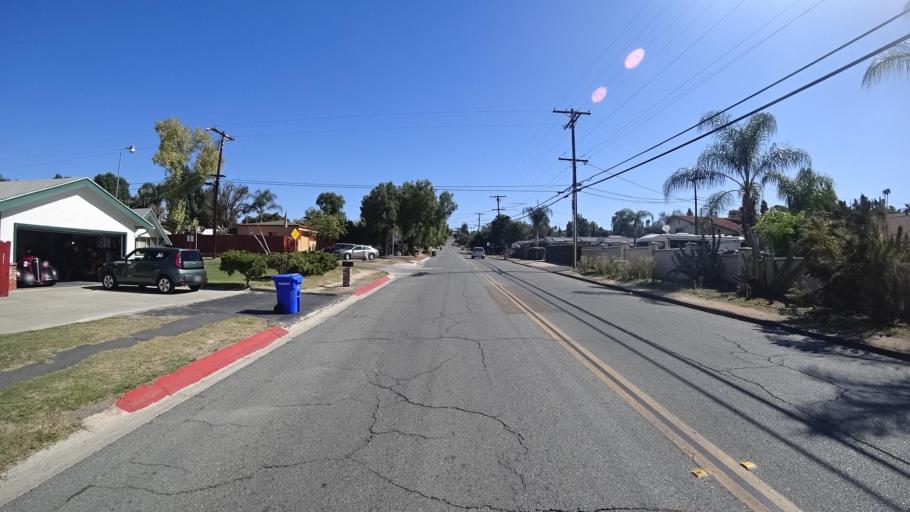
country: US
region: California
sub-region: San Diego County
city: Winter Gardens
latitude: 32.8208
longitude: -116.9284
